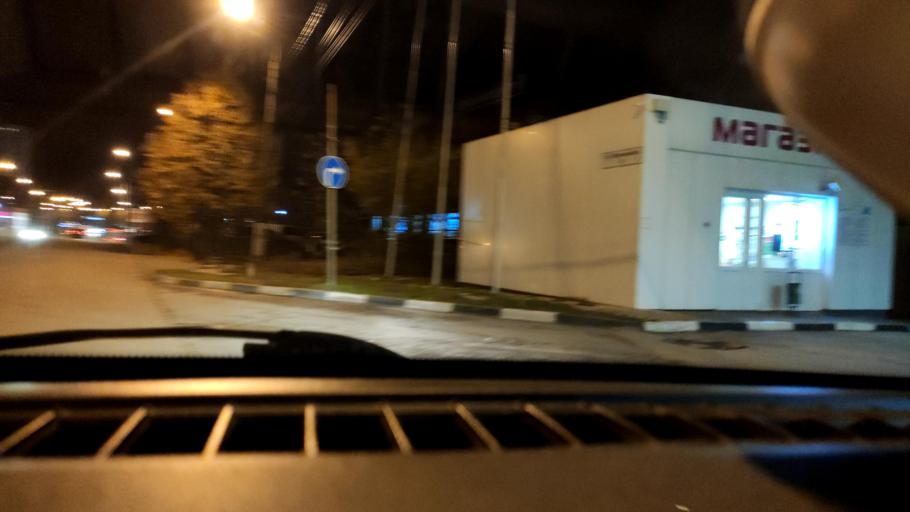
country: RU
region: Samara
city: Samara
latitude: 53.1936
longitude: 50.1642
